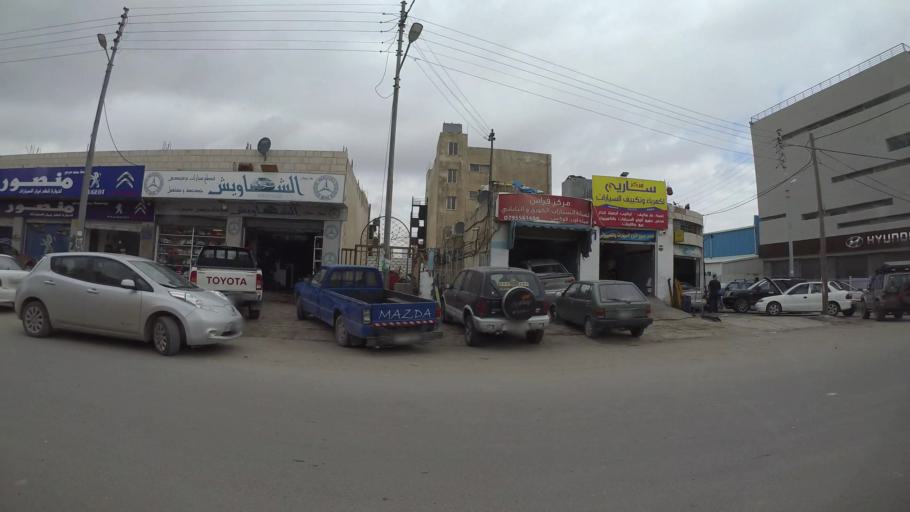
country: JO
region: Amman
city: Wadi as Sir
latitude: 31.9421
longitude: 35.8401
